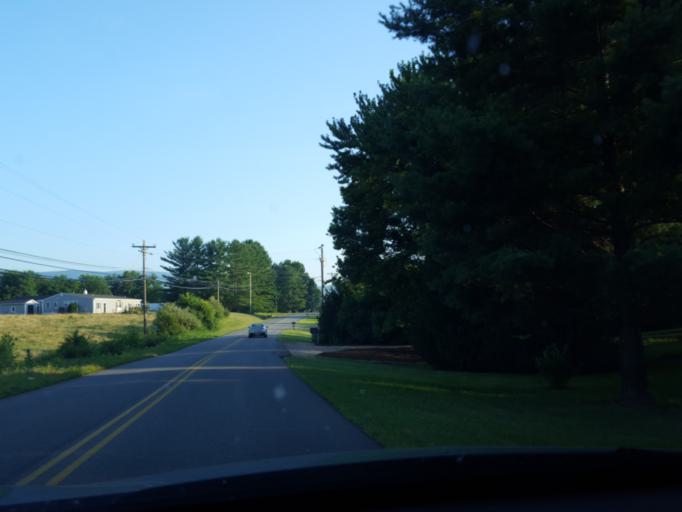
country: US
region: Virginia
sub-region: Augusta County
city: Lyndhurst
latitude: 38.0055
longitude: -78.9523
